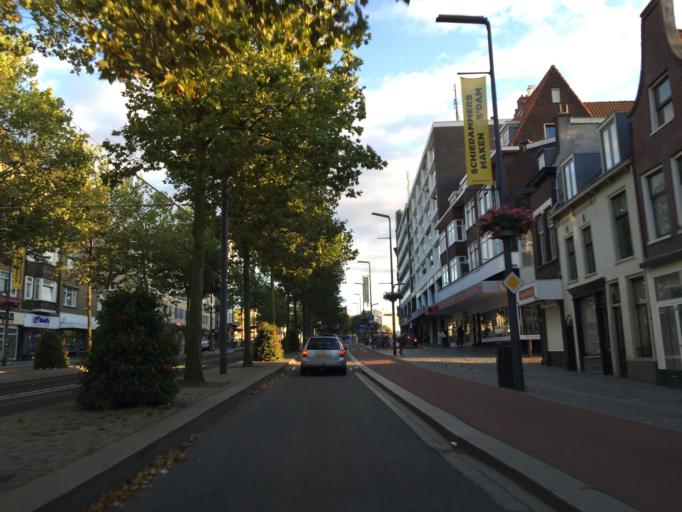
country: NL
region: South Holland
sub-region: Gemeente Schiedam
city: Schiedam
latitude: 51.9164
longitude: 4.4023
